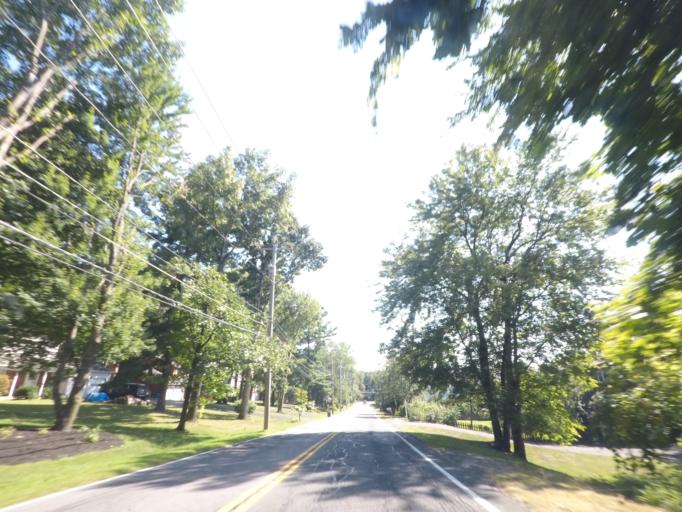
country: US
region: New York
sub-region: Albany County
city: Menands
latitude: 42.7025
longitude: -73.7422
